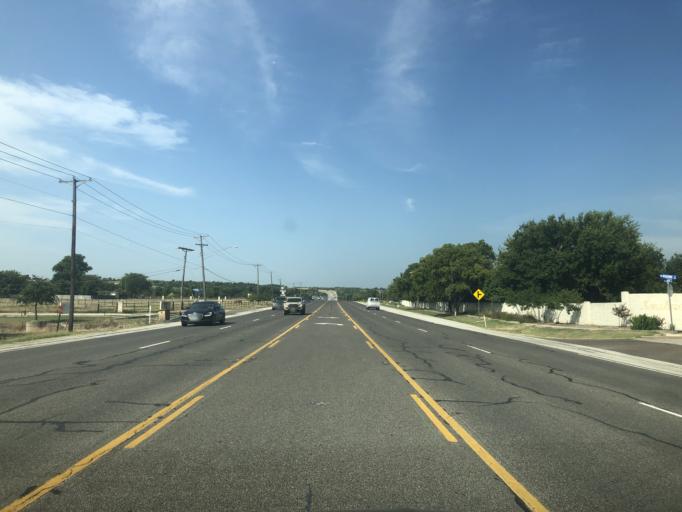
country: US
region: Texas
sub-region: Tarrant County
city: Benbrook
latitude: 32.6651
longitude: -97.4806
